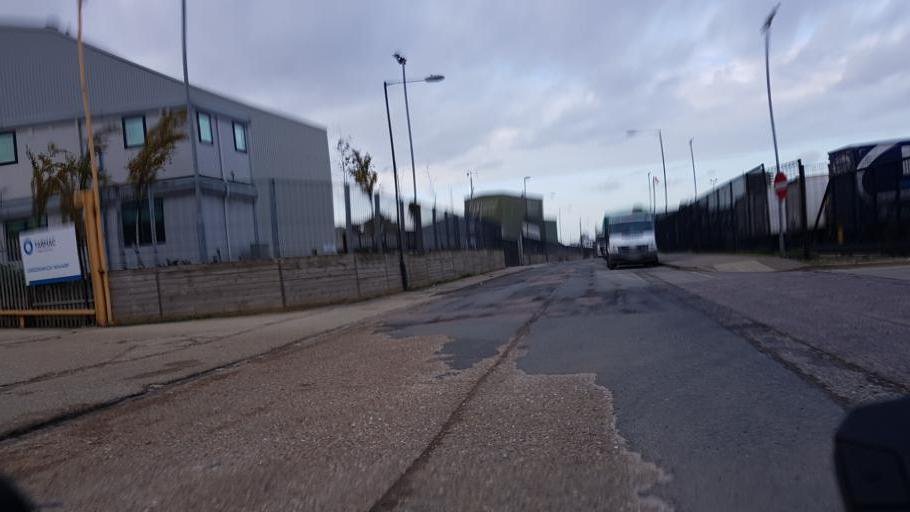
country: GB
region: England
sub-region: Greater London
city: Blackheath
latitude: 51.4913
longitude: 0.0248
